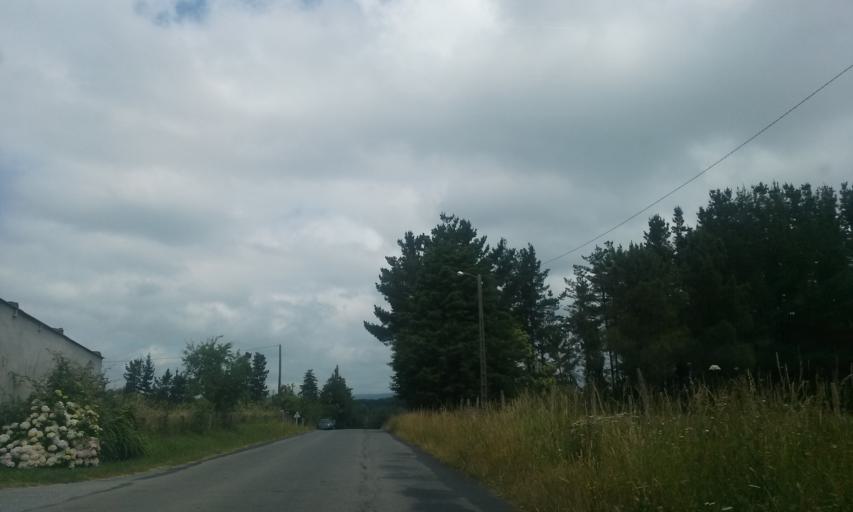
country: ES
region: Galicia
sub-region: Provincia de Lugo
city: Friol
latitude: 43.0877
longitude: -7.8098
